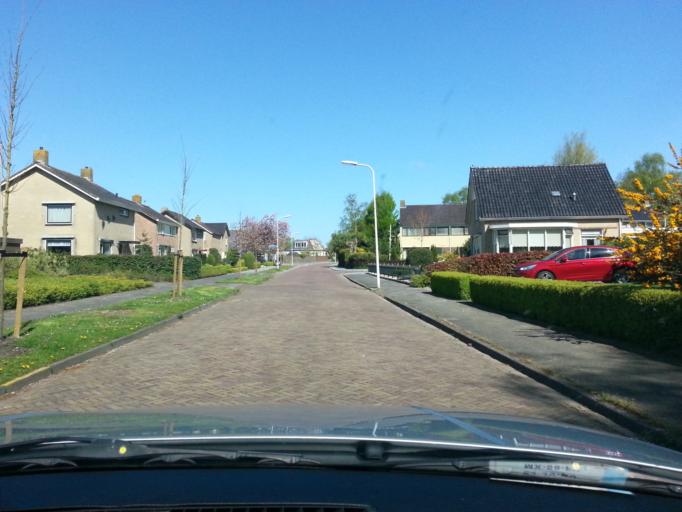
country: NL
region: Friesland
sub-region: Gemeente Achtkarspelen
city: Buitenpost
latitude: 53.2529
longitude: 6.1477
